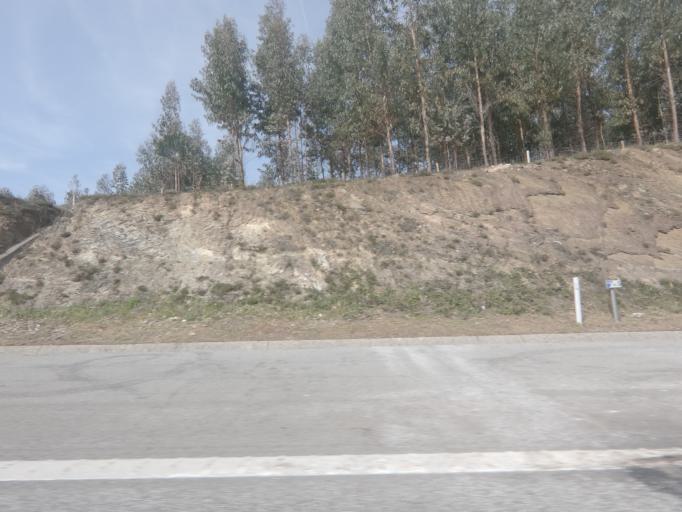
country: PT
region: Aveiro
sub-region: Agueda
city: Valongo
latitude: 40.6677
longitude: -8.4084
